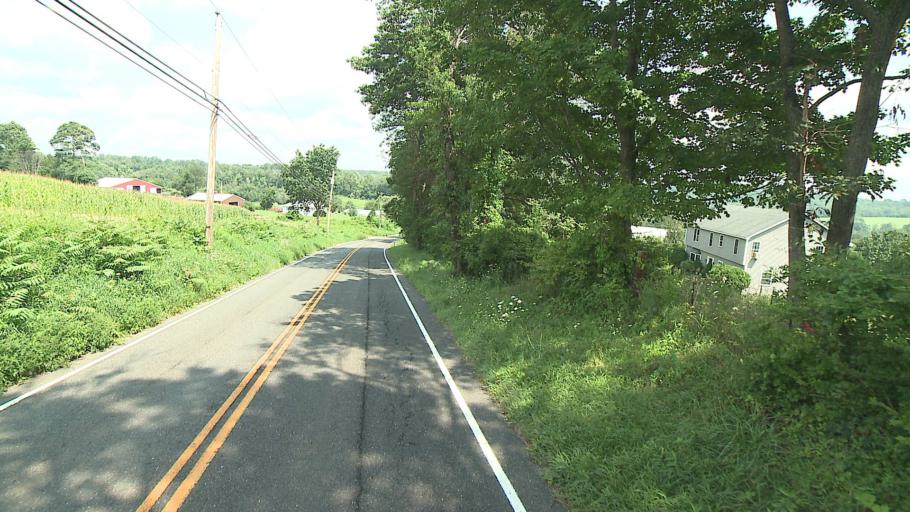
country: US
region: Connecticut
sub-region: Litchfield County
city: New Preston
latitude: 41.6289
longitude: -73.3659
